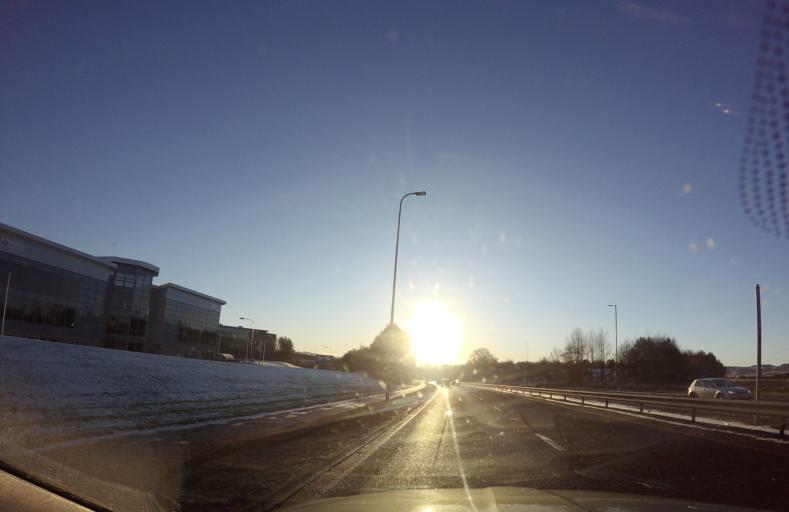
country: GB
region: Scotland
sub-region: Angus
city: Muirhead
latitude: 56.4710
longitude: -3.0569
